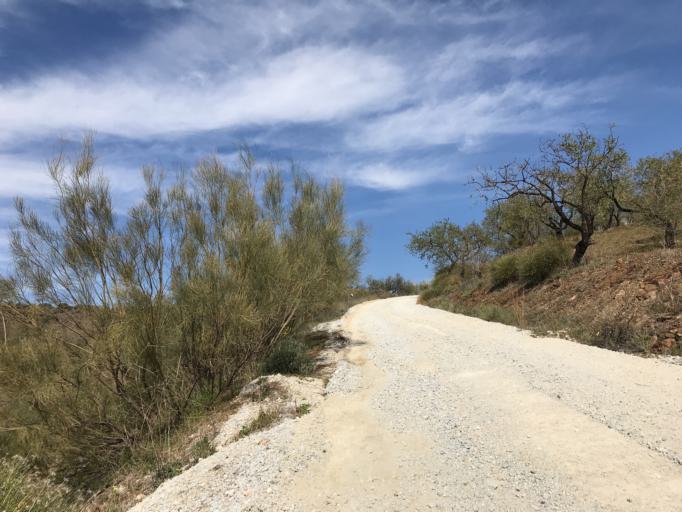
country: ES
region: Andalusia
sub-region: Provincia de Malaga
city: Valdes
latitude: 36.7773
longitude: -4.2182
